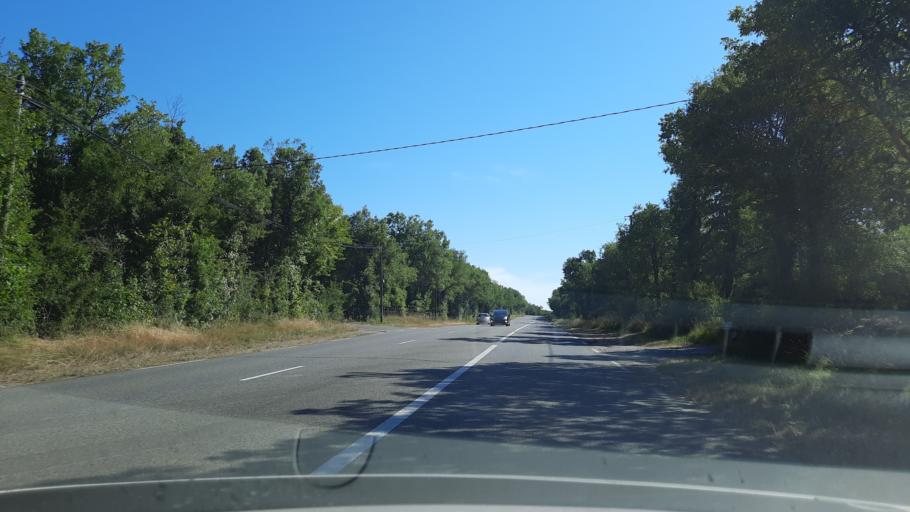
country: FR
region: Midi-Pyrenees
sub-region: Departement du Tarn-et-Garonne
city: Caylus
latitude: 44.2229
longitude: 1.7440
